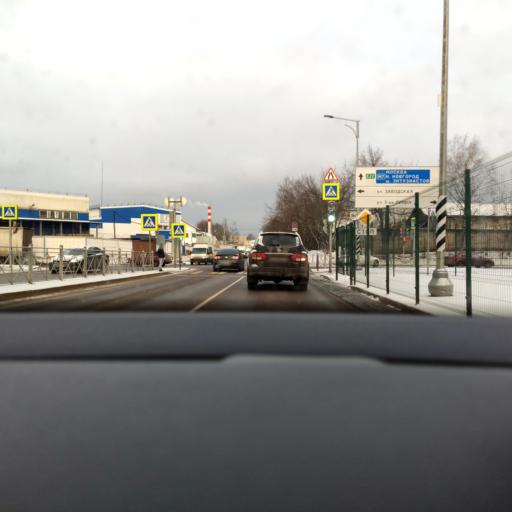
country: RU
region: Moskovskaya
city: Reutov
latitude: 55.7644
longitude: 37.8828
